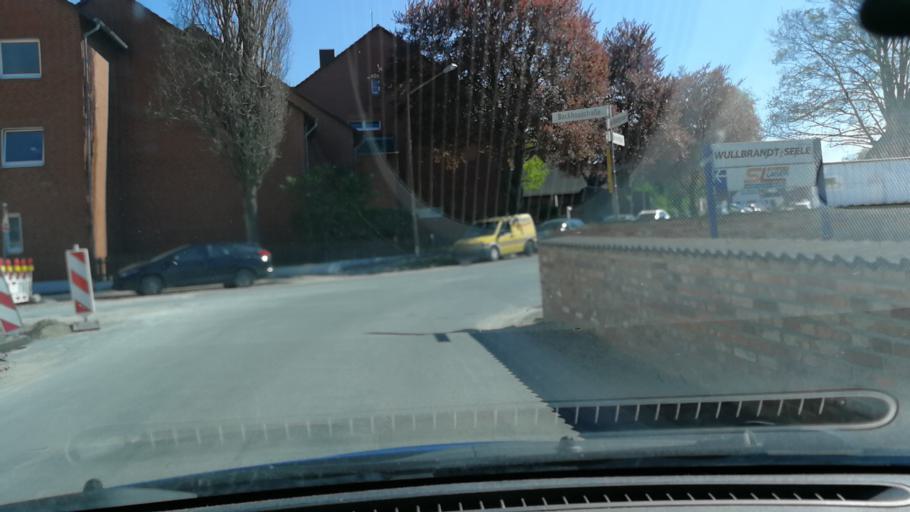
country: DE
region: Lower Saxony
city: Lehrte
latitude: 52.3660
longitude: 9.9120
